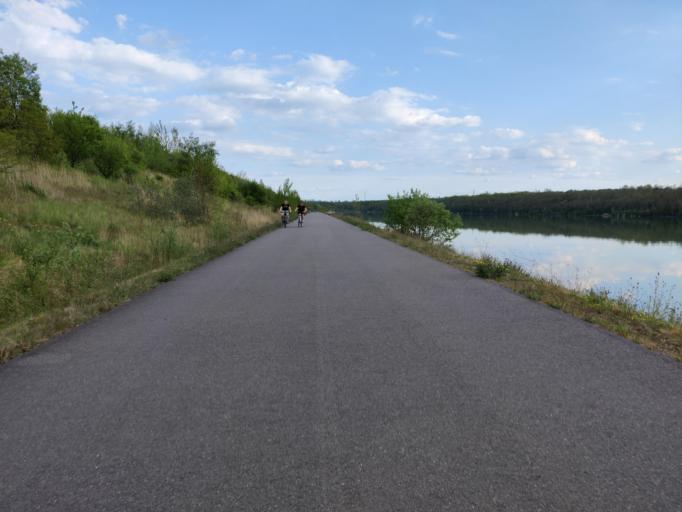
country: DE
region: Saxony
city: Rotha
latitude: 51.2174
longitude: 12.4449
